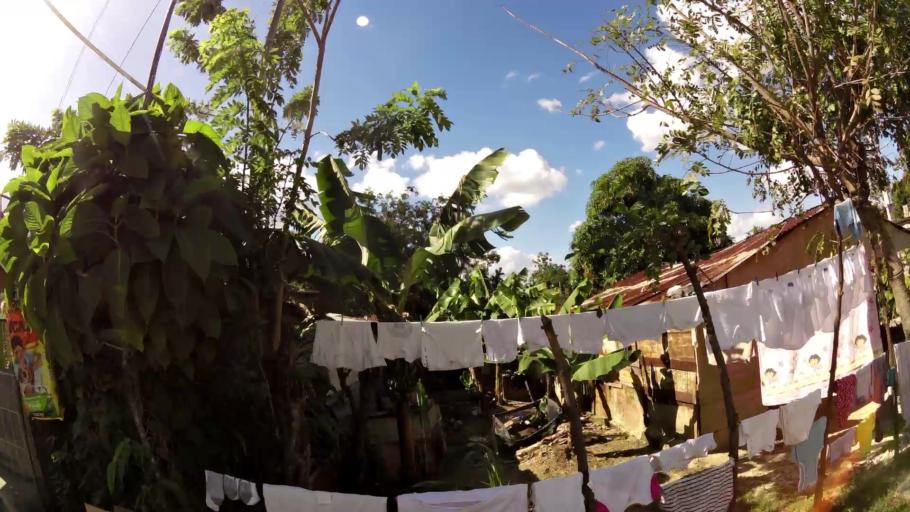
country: DO
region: Santo Domingo
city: Santo Domingo Oeste
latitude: 18.5409
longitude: -70.0385
